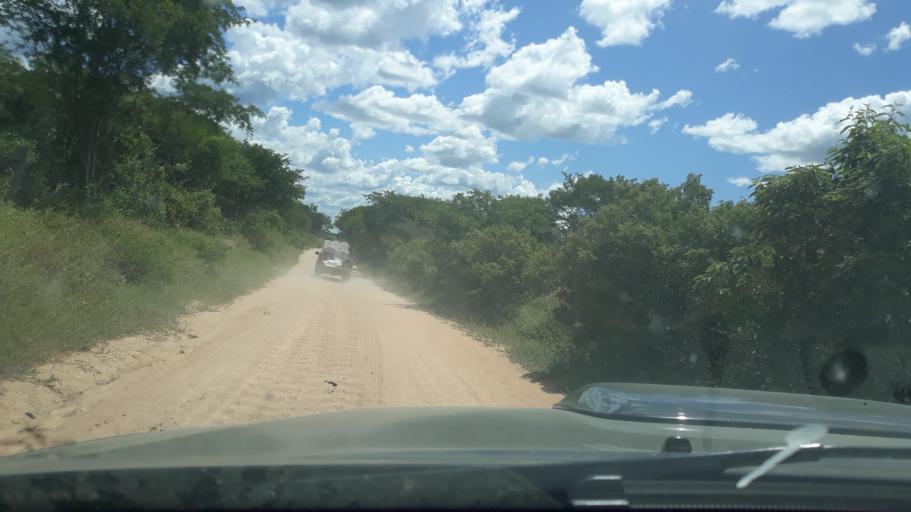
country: BR
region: Bahia
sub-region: Riacho De Santana
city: Riacho de Santana
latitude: -13.9090
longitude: -42.9441
